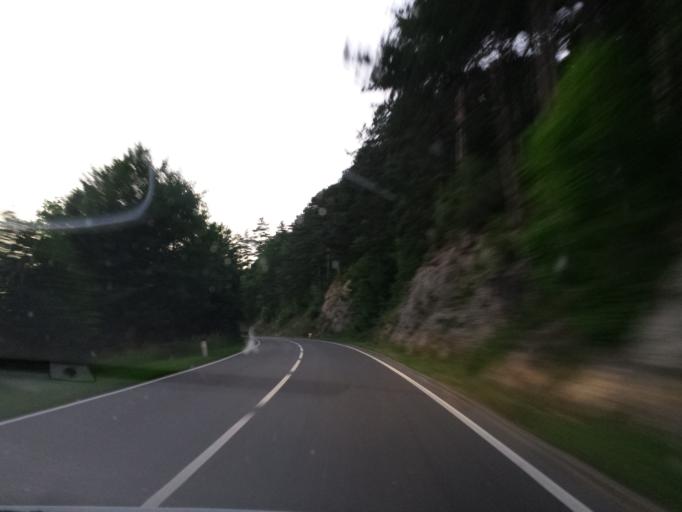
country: AT
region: Lower Austria
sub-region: Politischer Bezirk Baden
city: Altenmarkt an der Triesting
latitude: 48.0187
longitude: 16.0088
